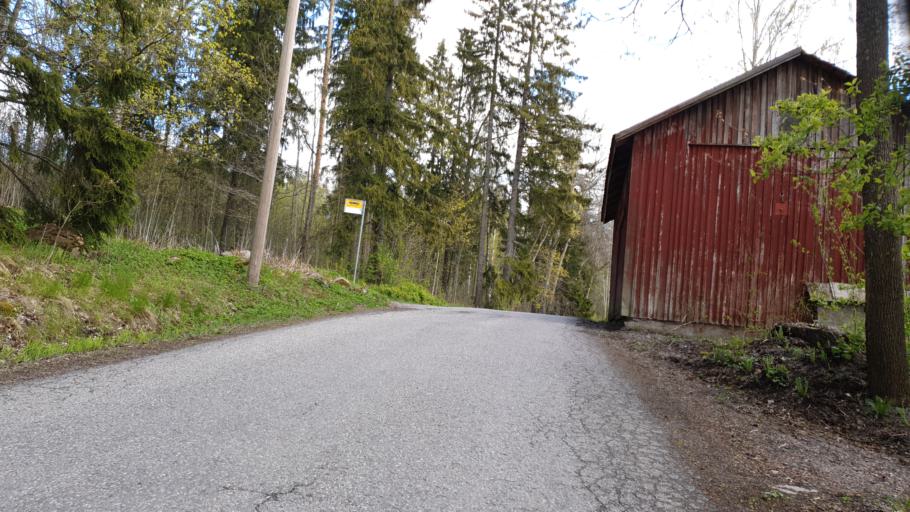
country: FI
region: Uusimaa
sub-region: Helsinki
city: Nurmijaervi
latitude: 60.3454
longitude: 24.8386
